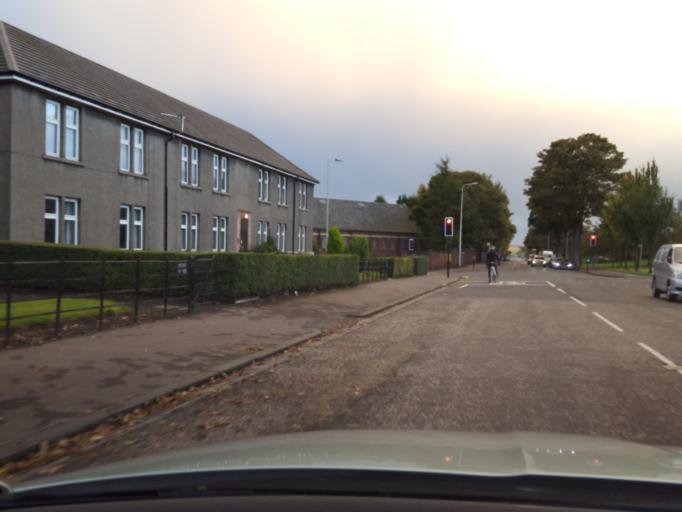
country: GB
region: Scotland
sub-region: Dundee City
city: Dundee
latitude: 56.4666
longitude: -3.0009
